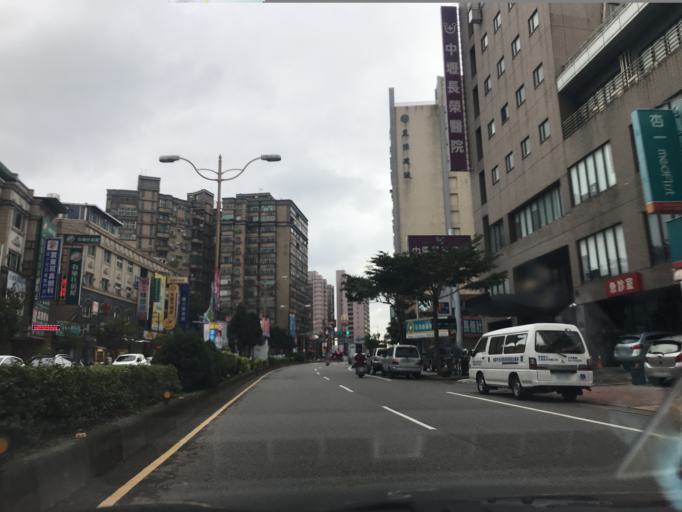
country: TW
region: Taiwan
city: Taoyuan City
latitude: 24.9648
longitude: 121.2584
